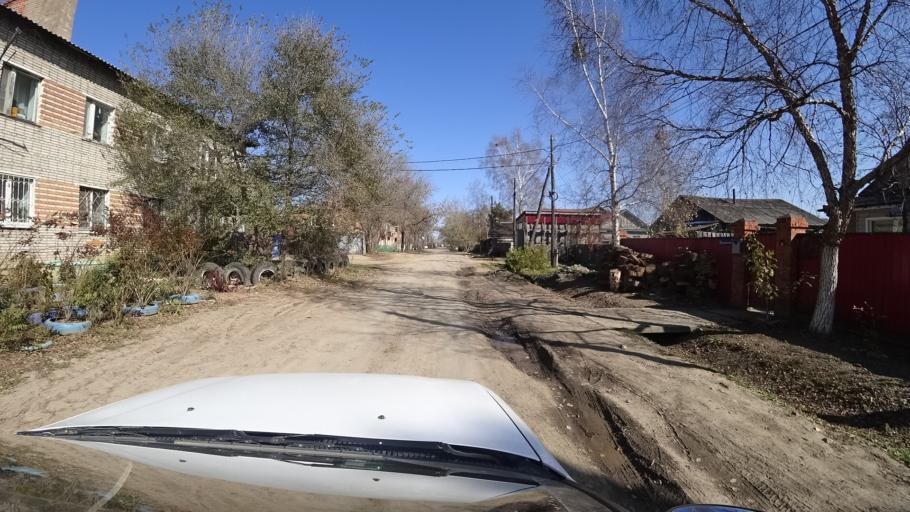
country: RU
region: Primorskiy
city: Dal'nerechensk
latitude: 45.9306
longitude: 133.7442
